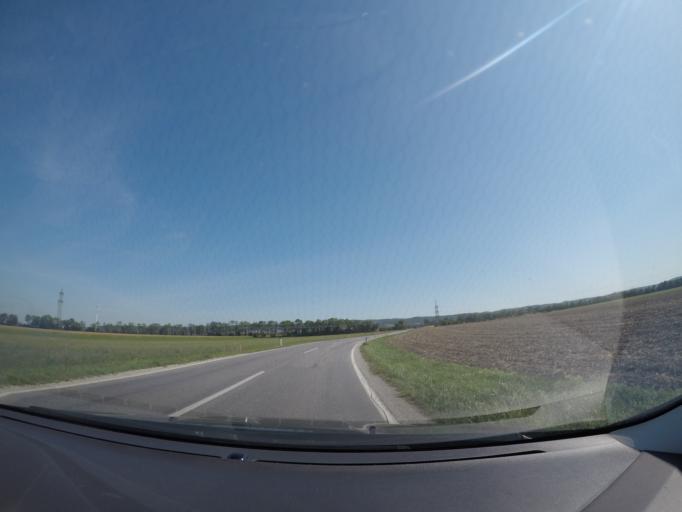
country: AT
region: Lower Austria
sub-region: Politischer Bezirk Baden
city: Seibersdorf
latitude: 47.9524
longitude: 16.5432
